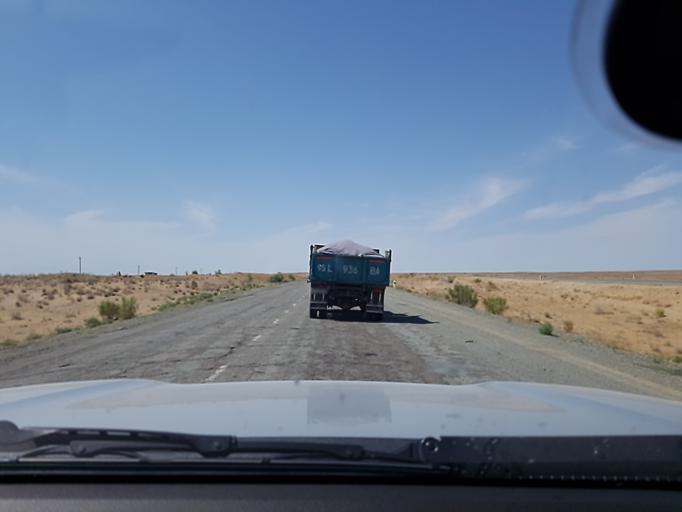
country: UZ
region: Karakalpakstan
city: Mang'it Shahri
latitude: 42.2877
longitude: 60.0773
